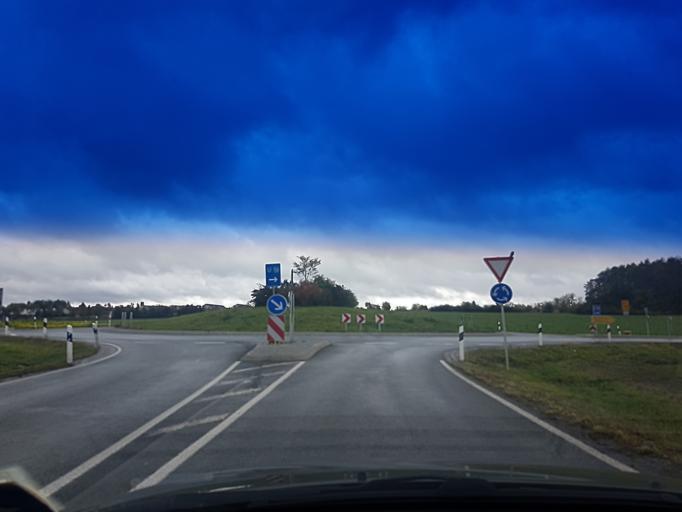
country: DE
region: Bavaria
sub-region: Upper Franconia
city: Bindlach
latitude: 50.0025
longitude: 11.6237
